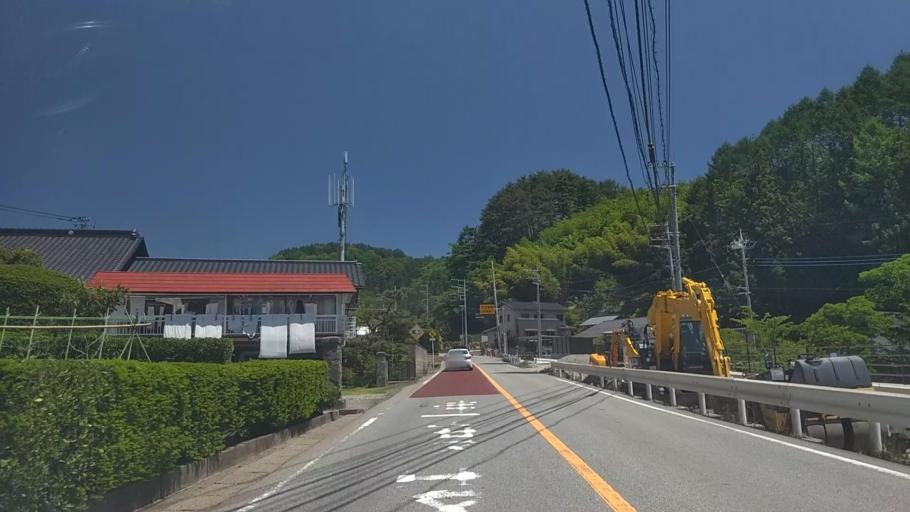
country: JP
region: Yamanashi
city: Nirasaki
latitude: 35.8715
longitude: 138.4281
